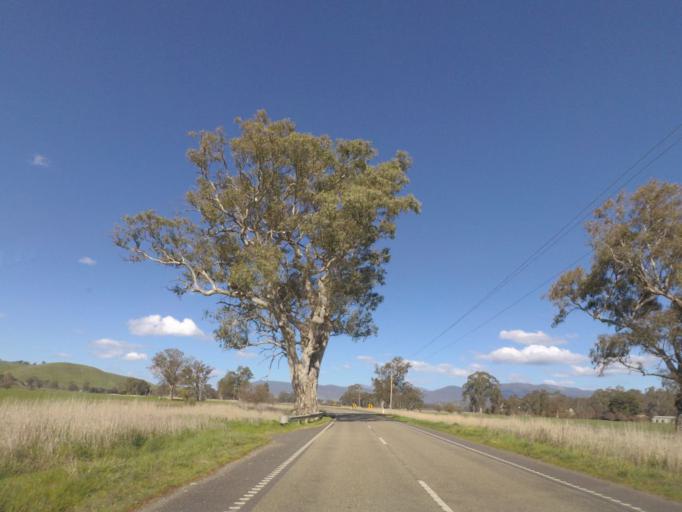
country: AU
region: Victoria
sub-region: Murrindindi
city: Alexandra
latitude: -37.2254
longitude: 145.7427
